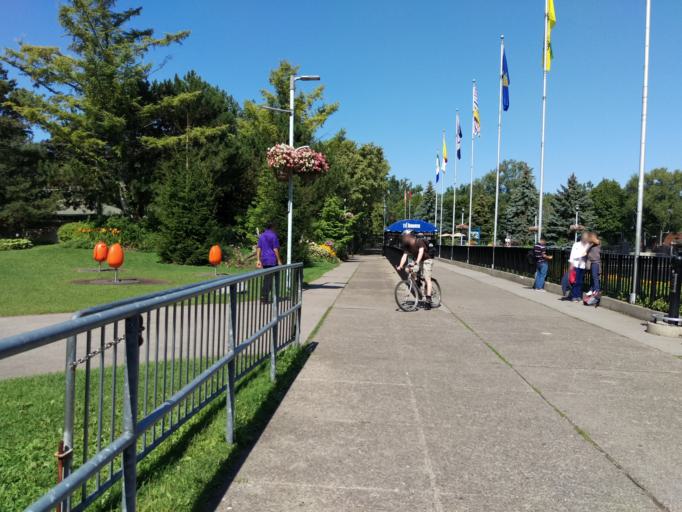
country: CA
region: Ontario
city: Toronto
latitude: 43.6220
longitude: -79.3775
